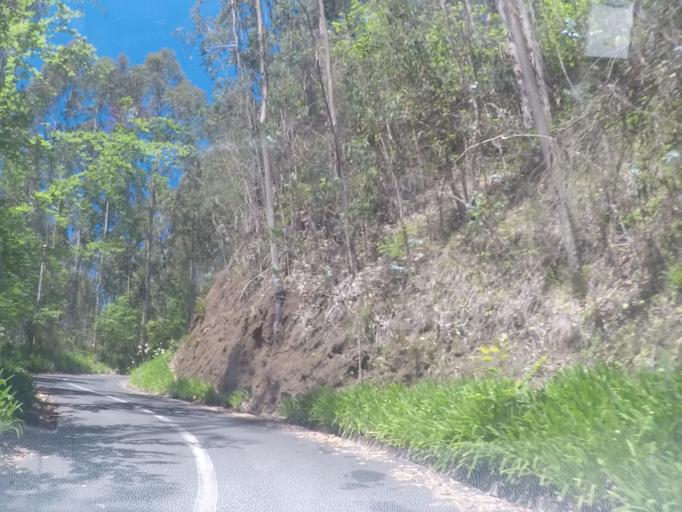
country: PT
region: Madeira
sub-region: Camara de Lobos
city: Curral das Freiras
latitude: 32.6936
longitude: -16.9773
